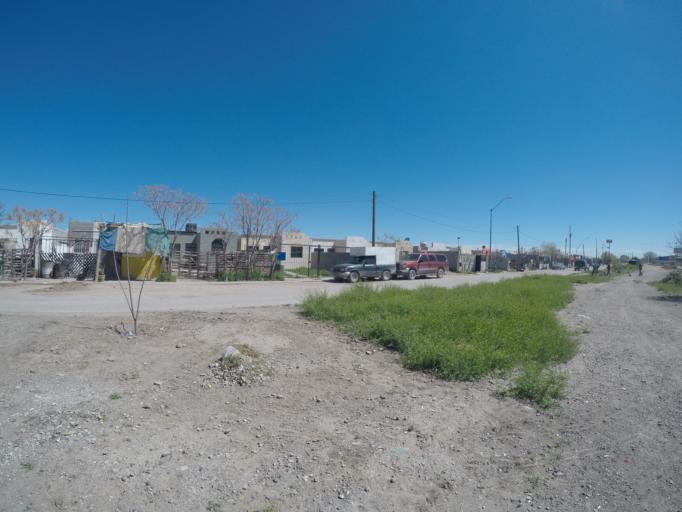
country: US
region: Texas
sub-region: El Paso County
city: Socorro Mission Number 1 Colonia
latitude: 31.6053
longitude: -106.3102
